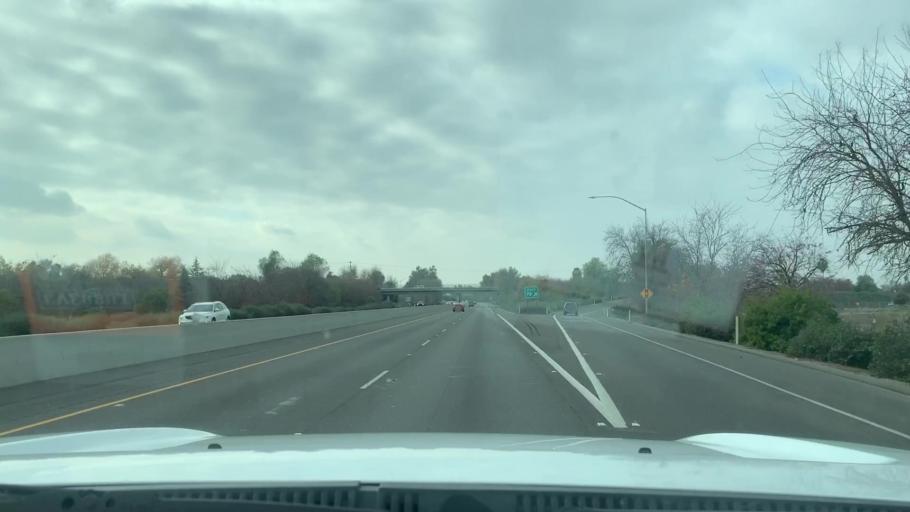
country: US
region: California
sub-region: Kings County
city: Lemoore
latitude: 36.2917
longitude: -119.7778
